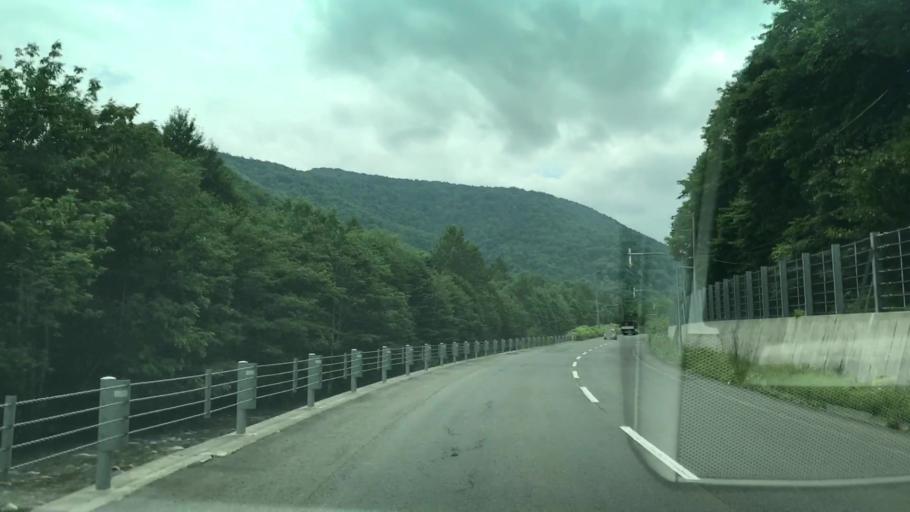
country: JP
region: Hokkaido
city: Yoichi
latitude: 43.0367
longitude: 140.8626
